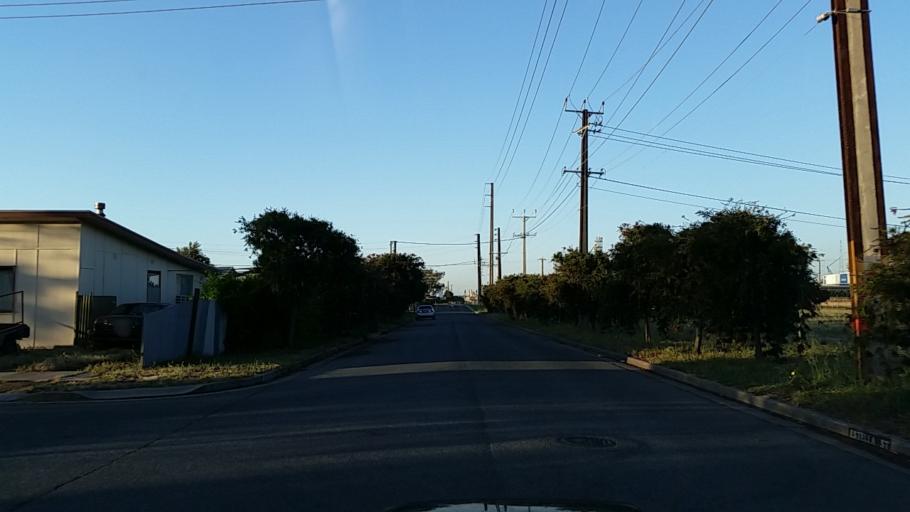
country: AU
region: South Australia
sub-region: Port Adelaide Enfield
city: Birkenhead
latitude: -34.7945
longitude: 138.5038
